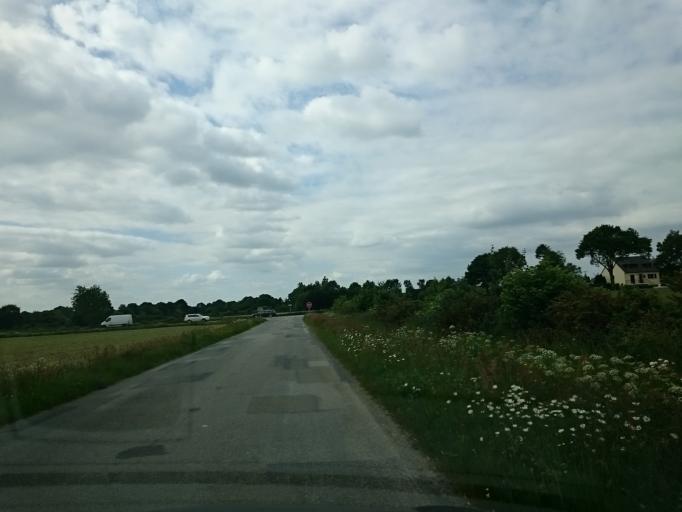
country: FR
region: Brittany
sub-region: Departement d'Ille-et-Vilaine
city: Chanteloup
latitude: 47.9398
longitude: -1.6336
